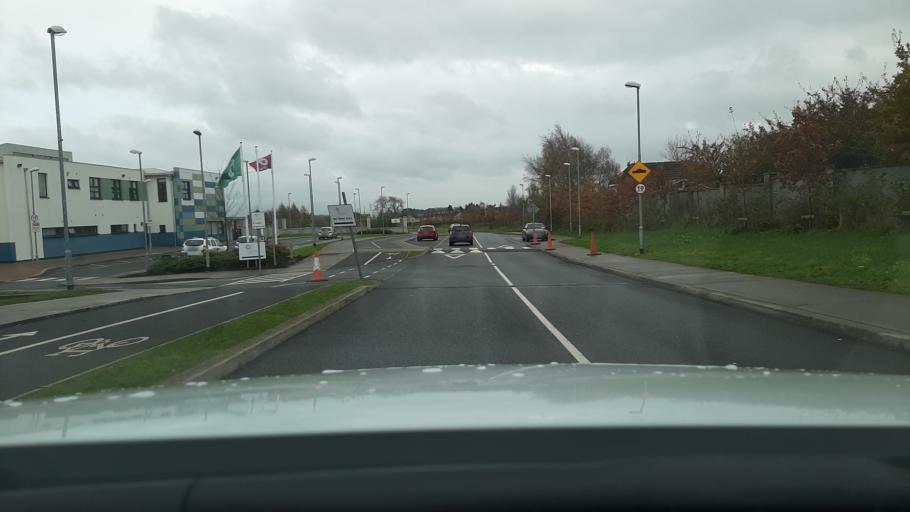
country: IE
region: Leinster
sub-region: Kildare
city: Kildare
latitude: 53.1595
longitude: -6.9034
